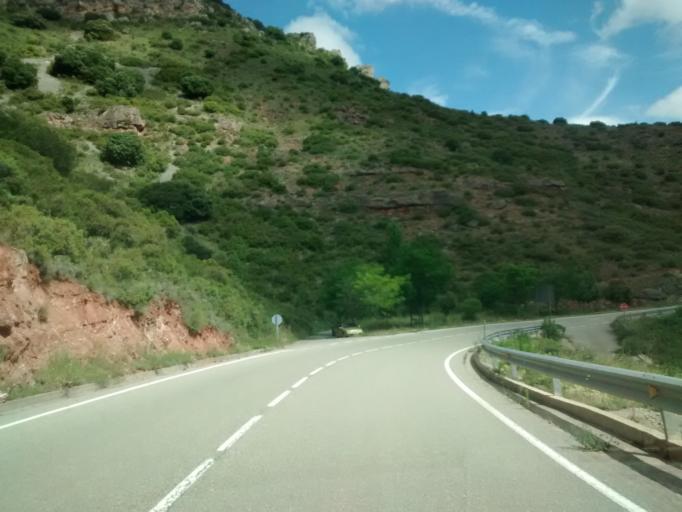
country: ES
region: La Rioja
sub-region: Provincia de La Rioja
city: Leza de Rio Leza
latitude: 42.3233
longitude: -2.4122
